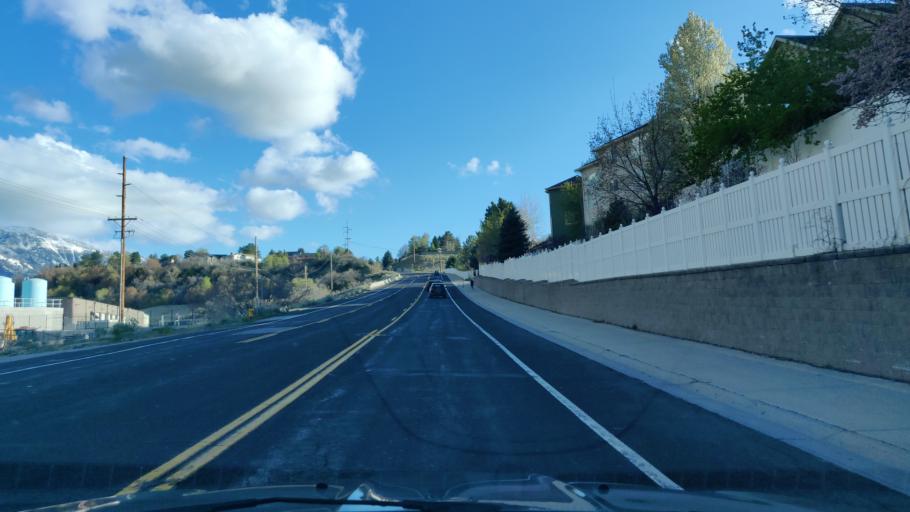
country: US
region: Utah
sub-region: Salt Lake County
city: Cottonwood Heights
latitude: 40.6312
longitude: -111.8071
